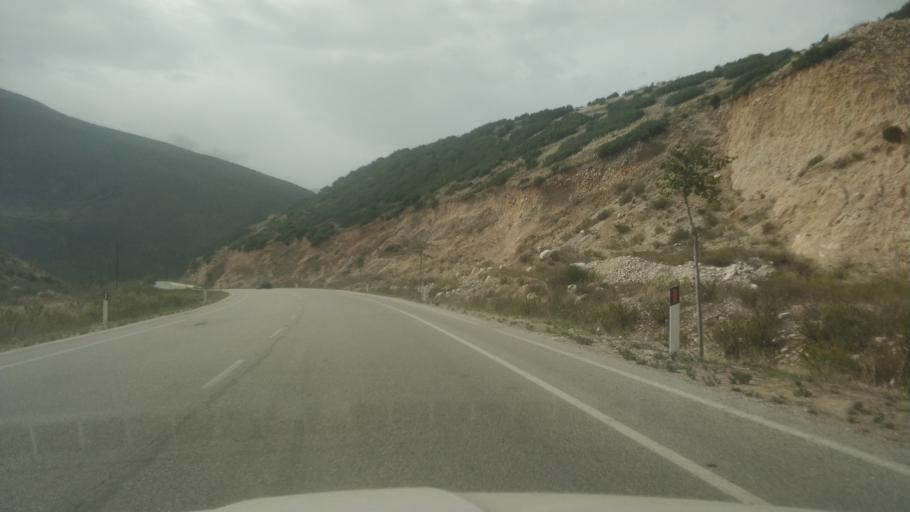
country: AL
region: Gjirokaster
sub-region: Rrethi i Tepelenes
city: Memaliaj
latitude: 40.3655
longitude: 19.9147
